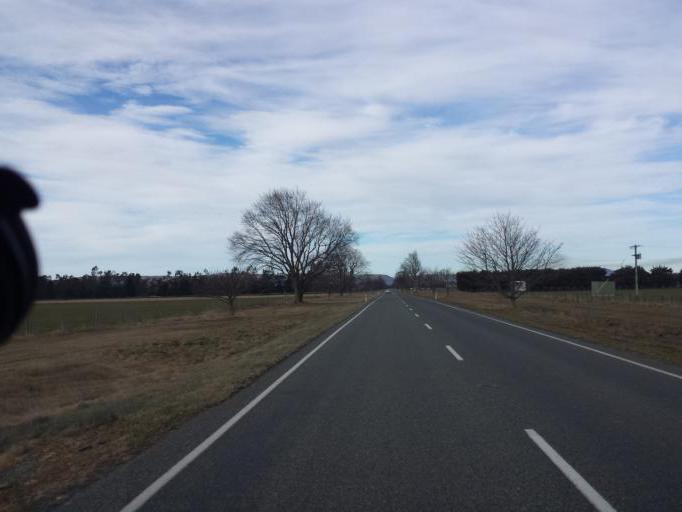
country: NZ
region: Canterbury
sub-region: Timaru District
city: Pleasant Point
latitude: -44.0685
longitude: 170.7884
